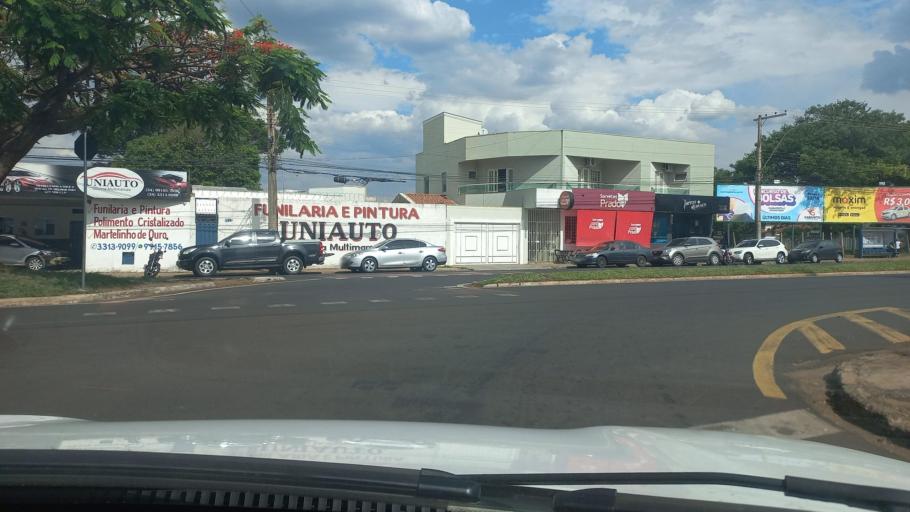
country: BR
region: Minas Gerais
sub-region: Uberaba
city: Uberaba
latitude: -19.7514
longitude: -47.9641
